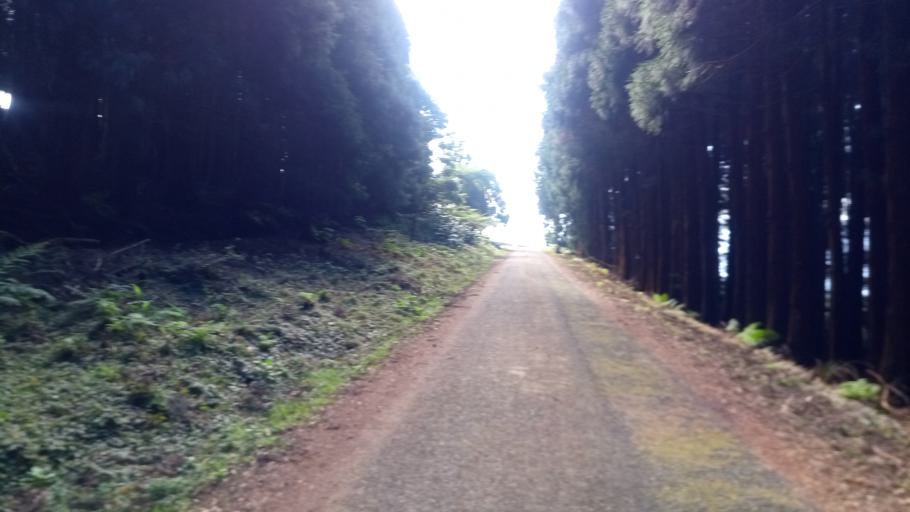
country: PT
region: Azores
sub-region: Praia da Vitoria
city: Biscoitos
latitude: 38.7142
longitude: -27.3290
